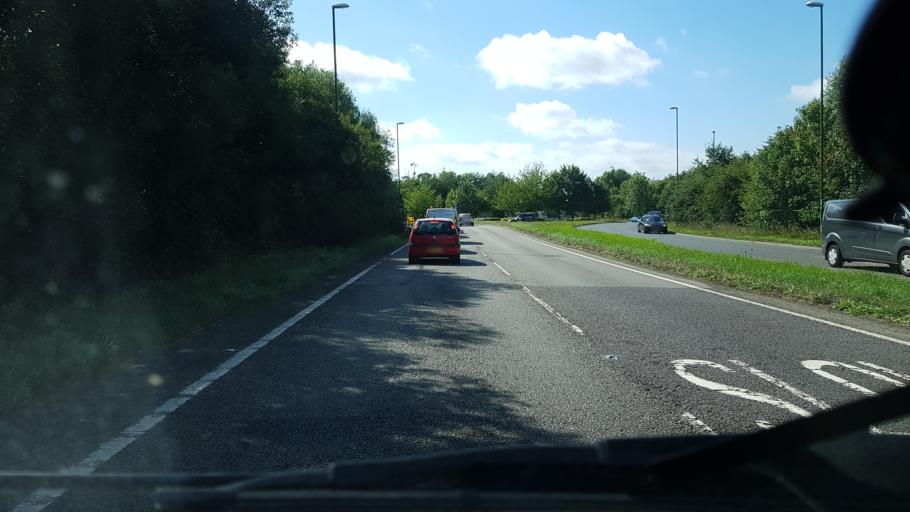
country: GB
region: England
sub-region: West Sussex
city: Horsham
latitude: 51.0875
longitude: -0.3312
